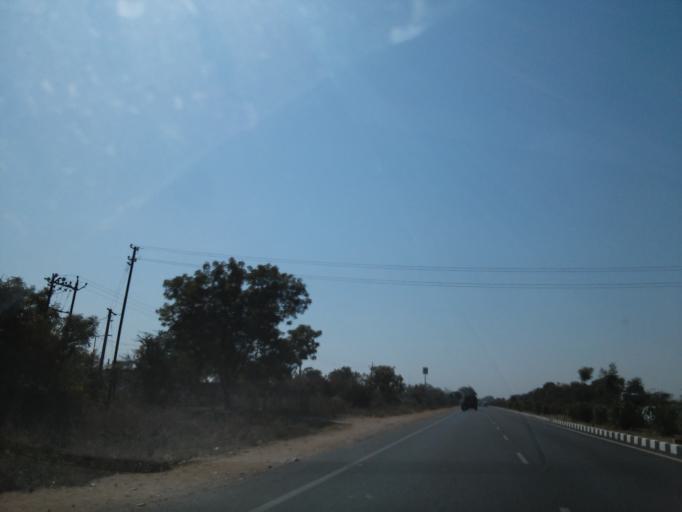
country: IN
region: Gujarat
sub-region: Sabar Kantha
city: Himatnagar
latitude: 23.5213
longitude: 72.9372
